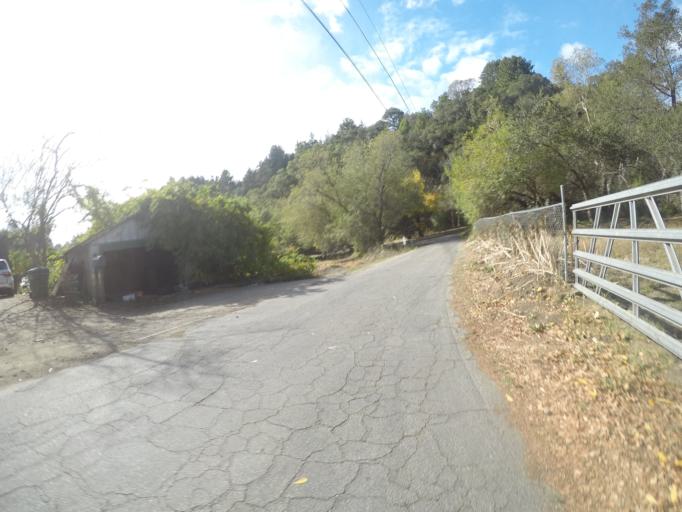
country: US
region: California
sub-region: Santa Cruz County
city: Soquel
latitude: 37.0350
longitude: -121.9672
